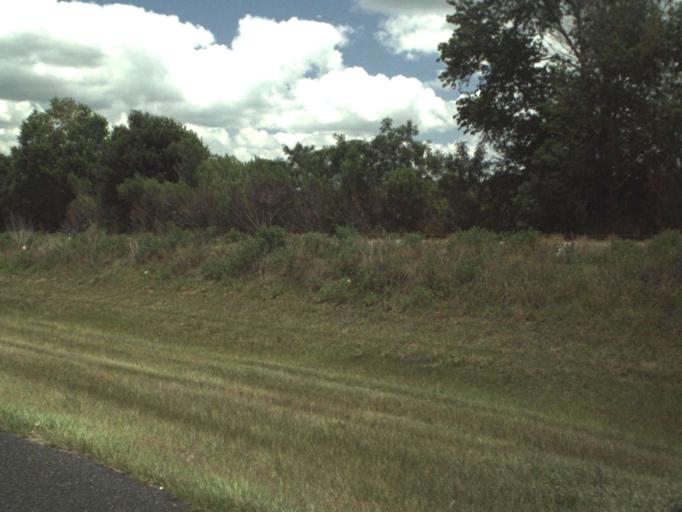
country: US
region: Florida
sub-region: Sumter County
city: The Villages
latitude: 28.9503
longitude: -82.0388
